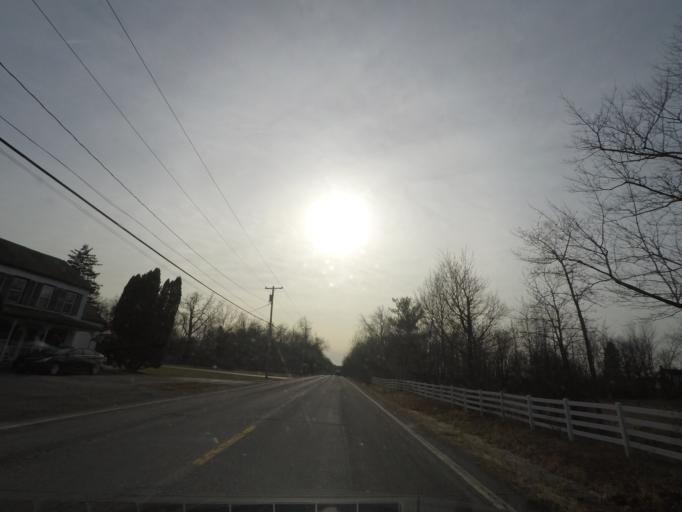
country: US
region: New York
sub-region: Saratoga County
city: Stillwater
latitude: 42.9675
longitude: -73.6335
